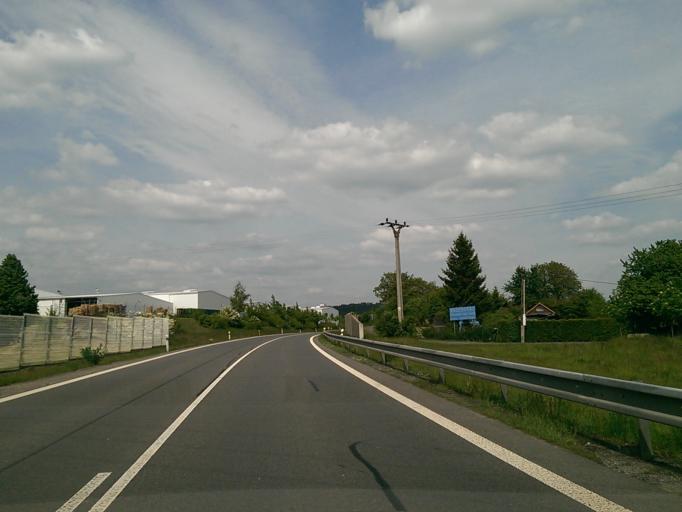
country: CZ
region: Liberecky
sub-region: Okres Semily
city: Turnov
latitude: 50.6007
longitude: 15.1480
